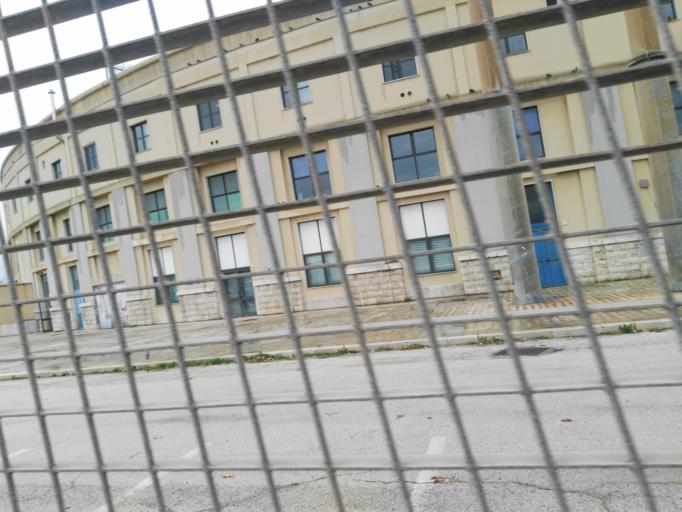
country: IT
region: Apulia
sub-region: Provincia di Bari
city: Bari
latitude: 41.1327
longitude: 16.8409
